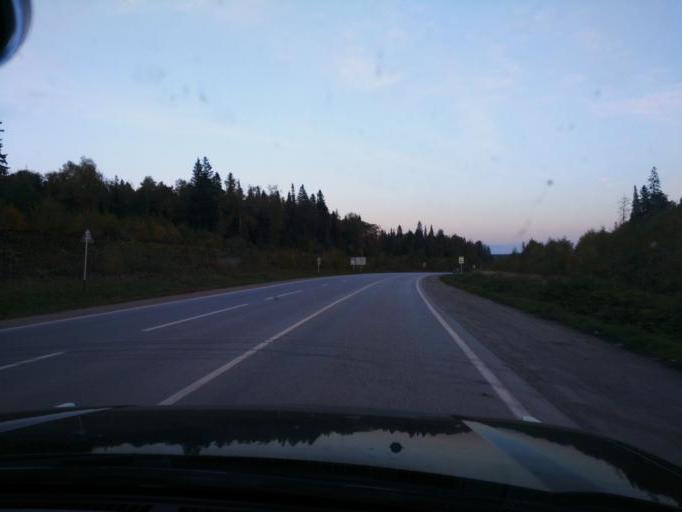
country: RU
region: Perm
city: Polazna
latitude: 58.2940
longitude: 56.4844
